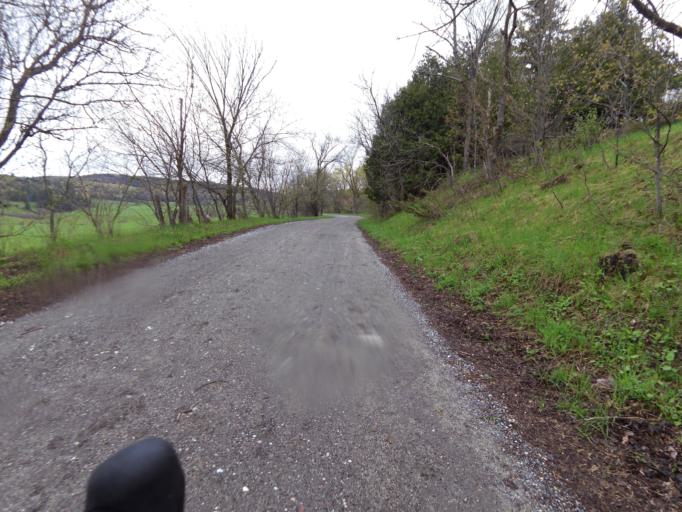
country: CA
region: Quebec
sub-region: Outaouais
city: Wakefield
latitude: 45.5810
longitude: -75.8921
